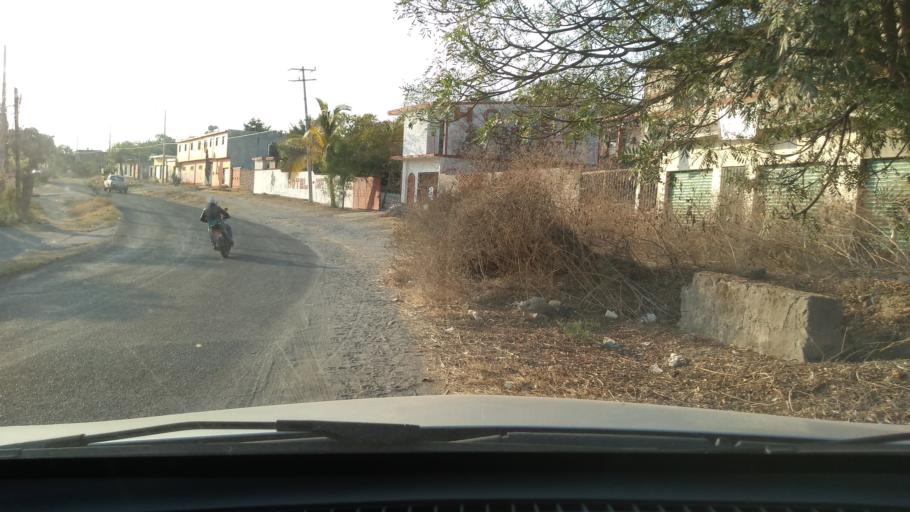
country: MX
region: Morelos
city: Puente de Ixtla
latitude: 18.6065
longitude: -99.3153
